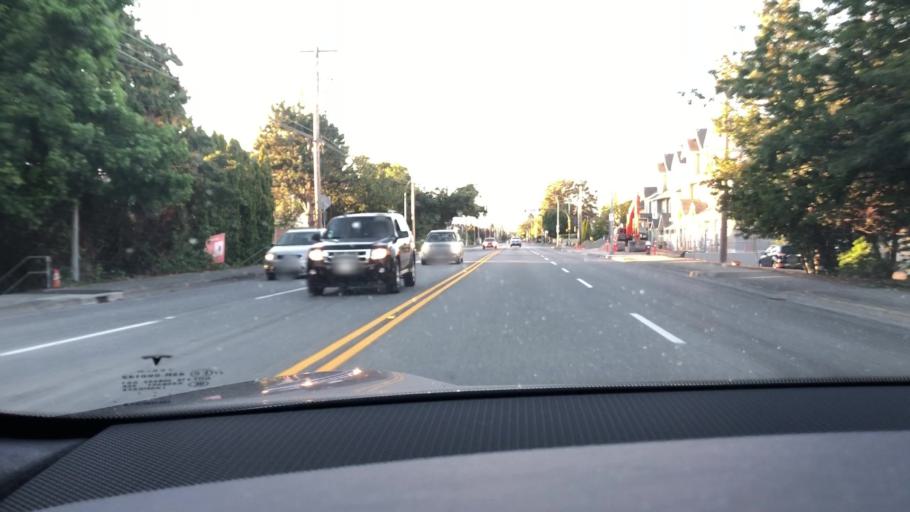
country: CA
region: British Columbia
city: Richmond
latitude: 49.1470
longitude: -123.1590
